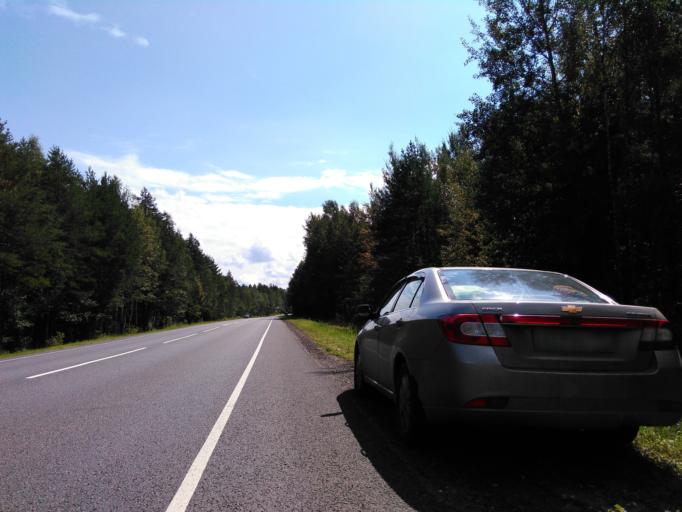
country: RU
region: Moskovskaya
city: Elektrogorsk
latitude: 56.0266
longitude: 38.7572
